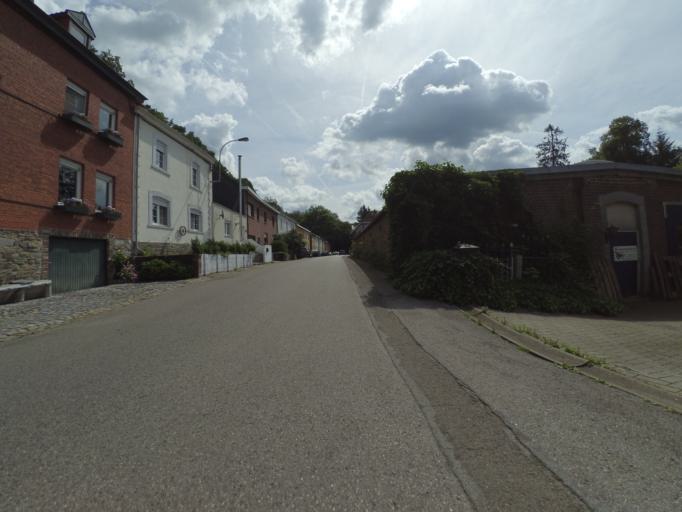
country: BE
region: Wallonia
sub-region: Province de Liege
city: Eupen
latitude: 50.6197
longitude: 6.0540
